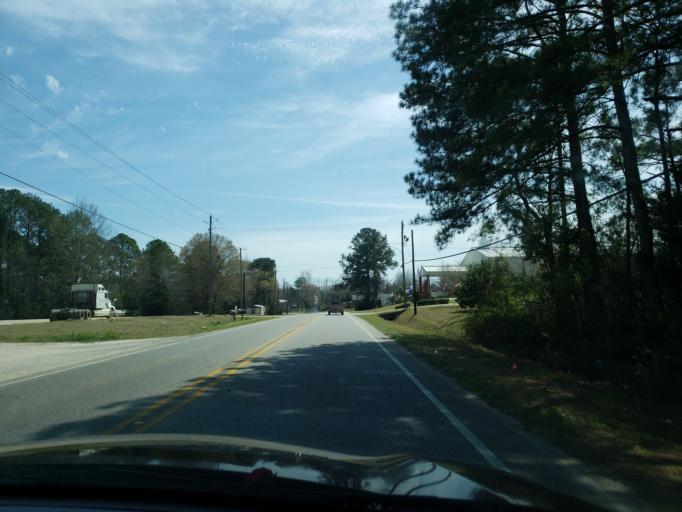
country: US
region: Alabama
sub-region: Elmore County
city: Tallassee
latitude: 32.5618
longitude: -85.9294
